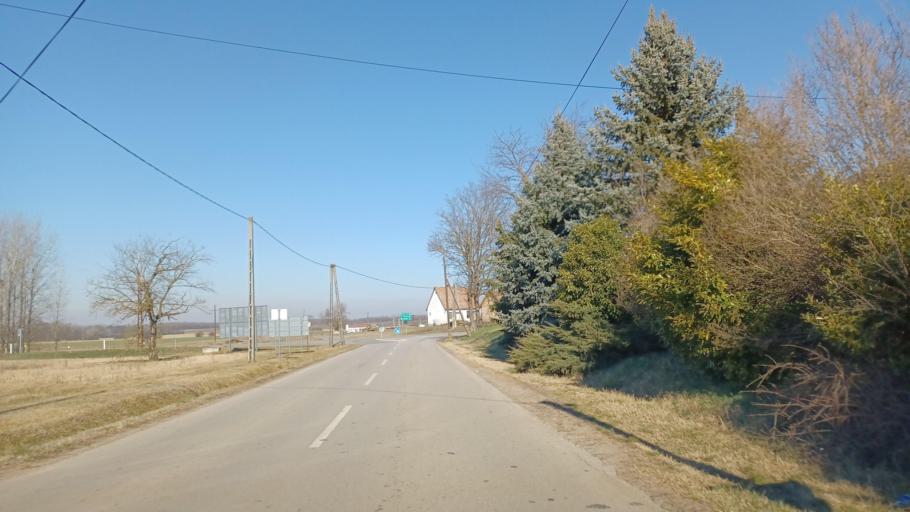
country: HU
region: Tolna
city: Tengelic
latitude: 46.5458
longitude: 18.6991
